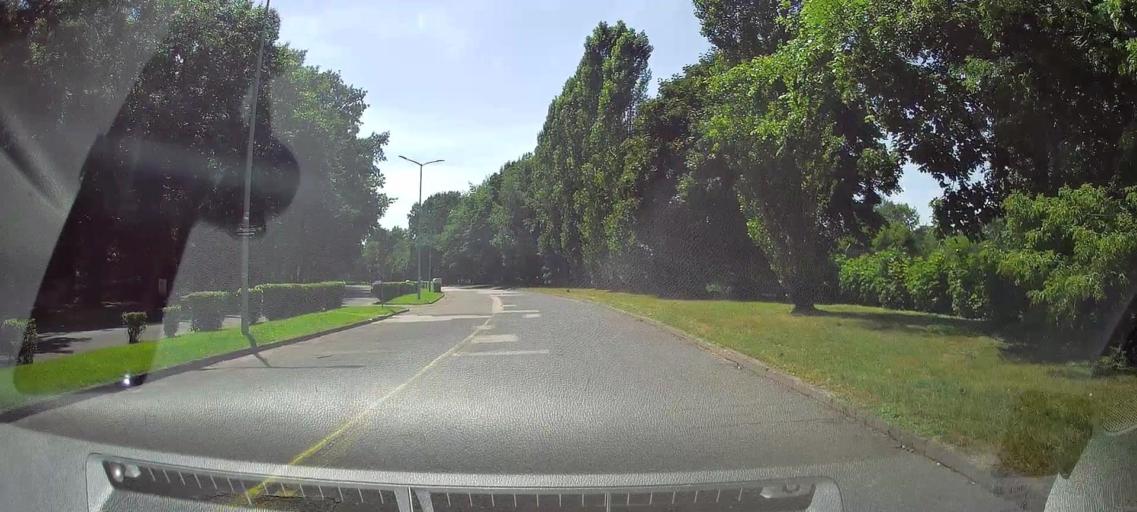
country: PL
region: Masovian Voivodeship
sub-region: Warszawa
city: Mokotow
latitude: 52.1648
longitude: 21.0103
